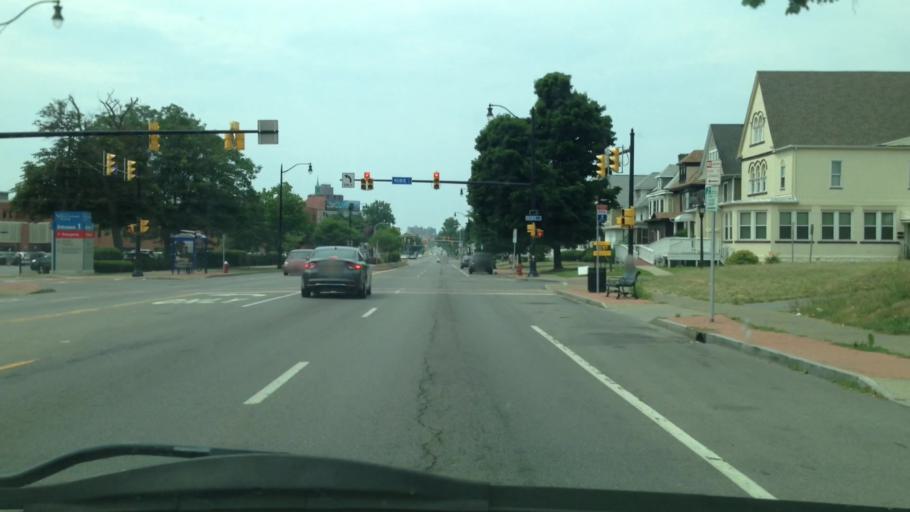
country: US
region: New York
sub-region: Erie County
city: Kenmore
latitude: 42.9299
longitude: -78.8493
